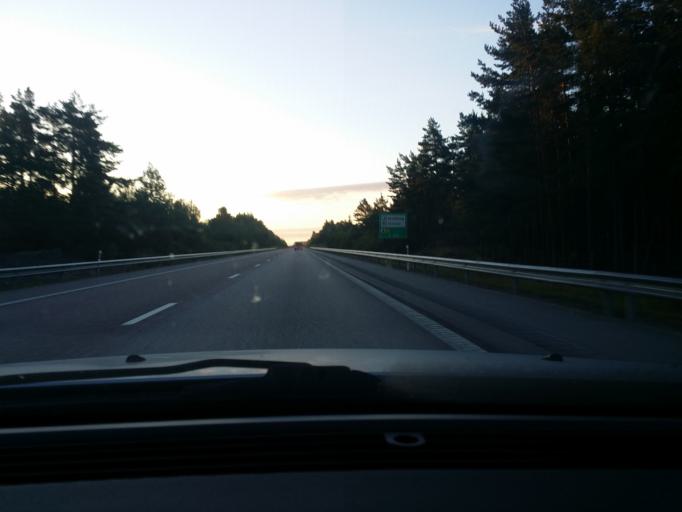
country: SE
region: Uppsala
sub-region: Enkopings Kommun
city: Grillby
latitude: 59.6294
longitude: 17.3412
